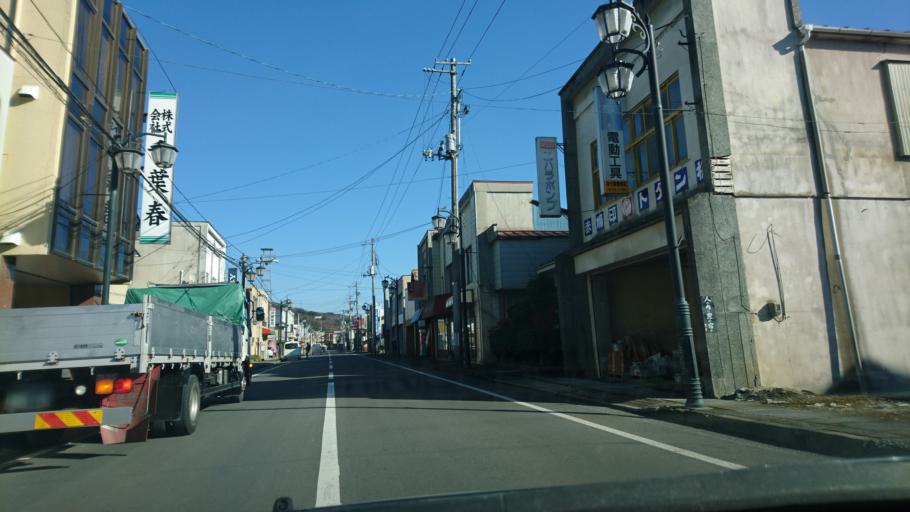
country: JP
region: Iwate
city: Ichinoseki
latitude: 38.9906
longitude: 141.2503
